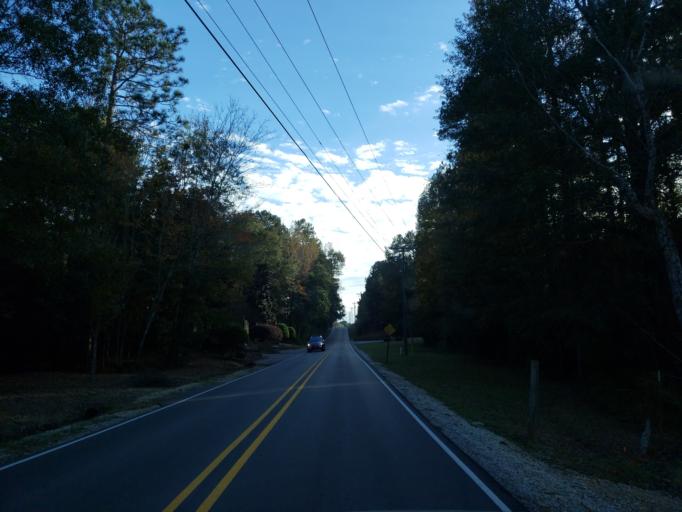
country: US
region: Mississippi
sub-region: Lamar County
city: West Hattiesburg
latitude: 31.2994
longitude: -89.3988
